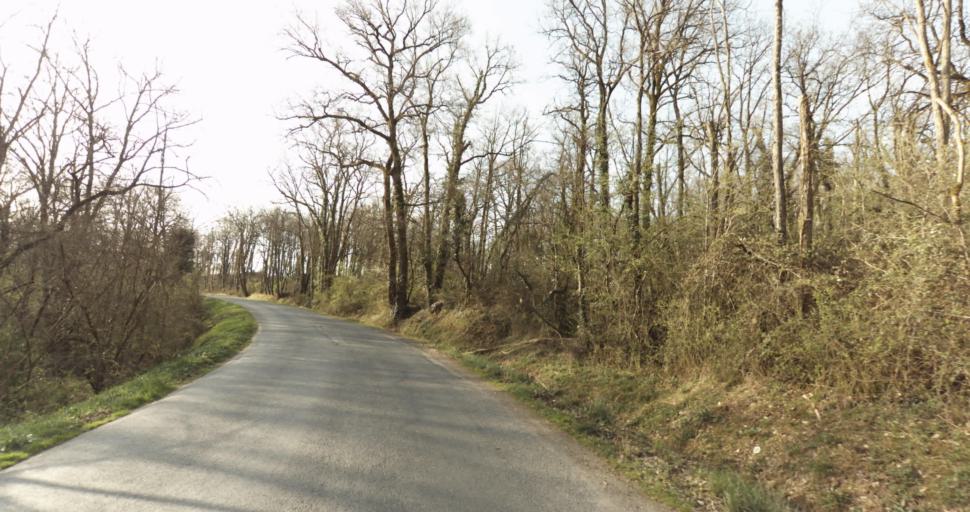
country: FR
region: Midi-Pyrenees
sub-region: Departement du Tarn
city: Saint-Sulpice-la-Pointe
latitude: 43.7486
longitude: 1.6879
